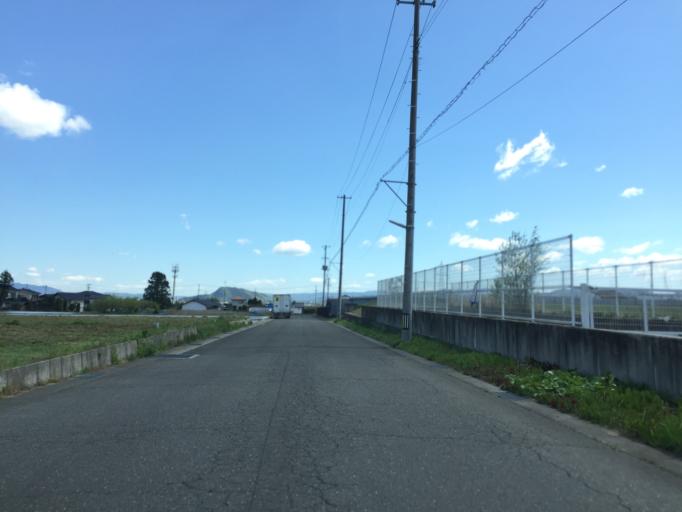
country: JP
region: Fukushima
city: Fukushima-shi
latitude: 37.7304
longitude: 140.3940
